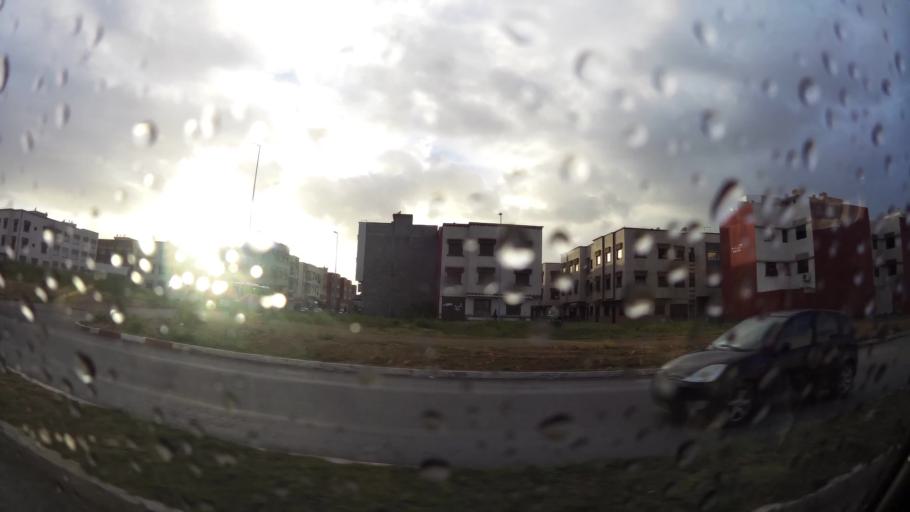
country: MA
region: Doukkala-Abda
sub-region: El-Jadida
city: El Jadida
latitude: 33.2341
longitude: -8.4848
